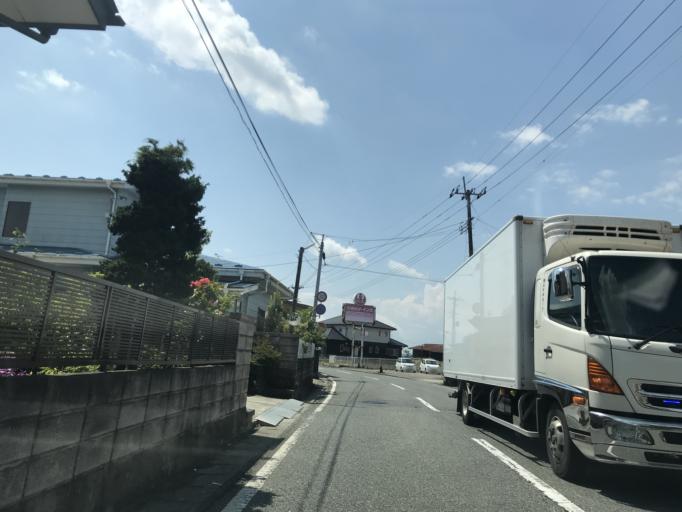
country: JP
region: Miyagi
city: Kogota
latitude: 38.5967
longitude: 141.0256
